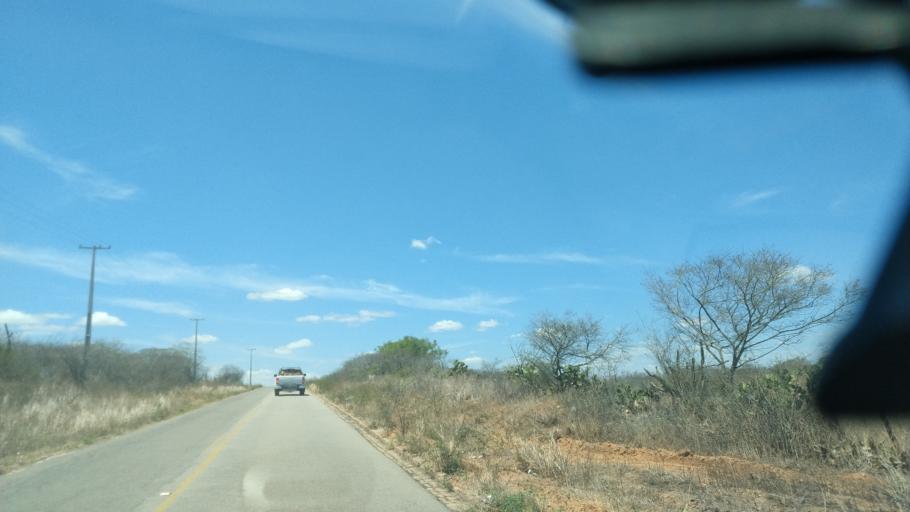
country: BR
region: Rio Grande do Norte
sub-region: Sao Paulo Do Potengi
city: Sao Paulo do Potengi
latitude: -5.9019
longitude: -35.6157
